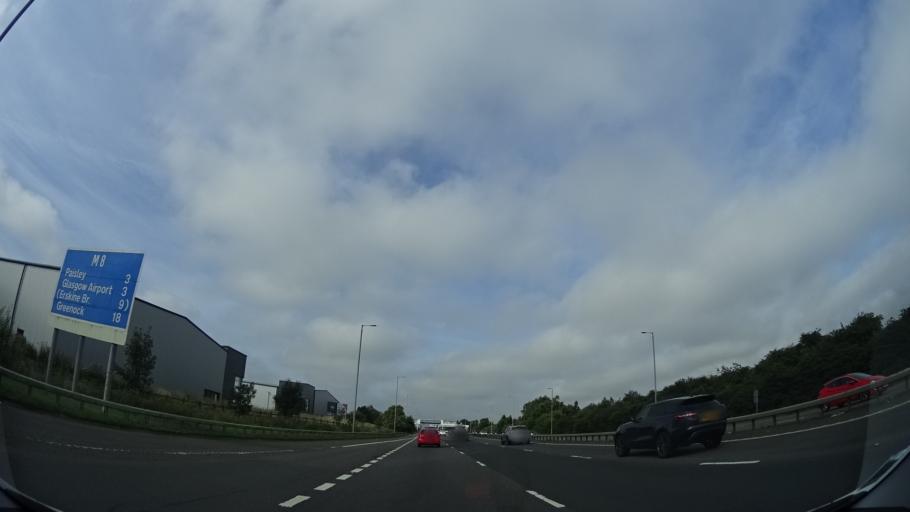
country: GB
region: Scotland
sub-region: Renfrewshire
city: Renfrew
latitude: 55.8653
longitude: -4.3786
